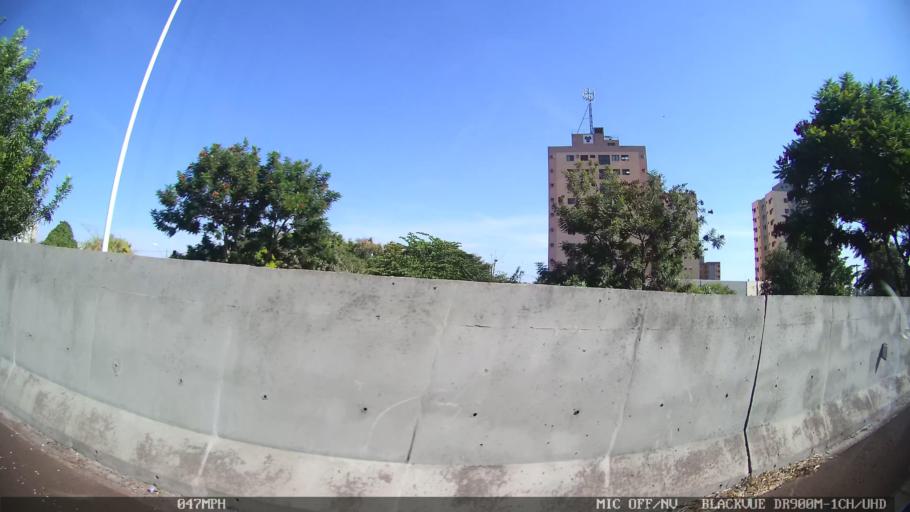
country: BR
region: Sao Paulo
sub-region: Ribeirao Preto
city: Ribeirao Preto
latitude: -21.1900
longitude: -47.7809
